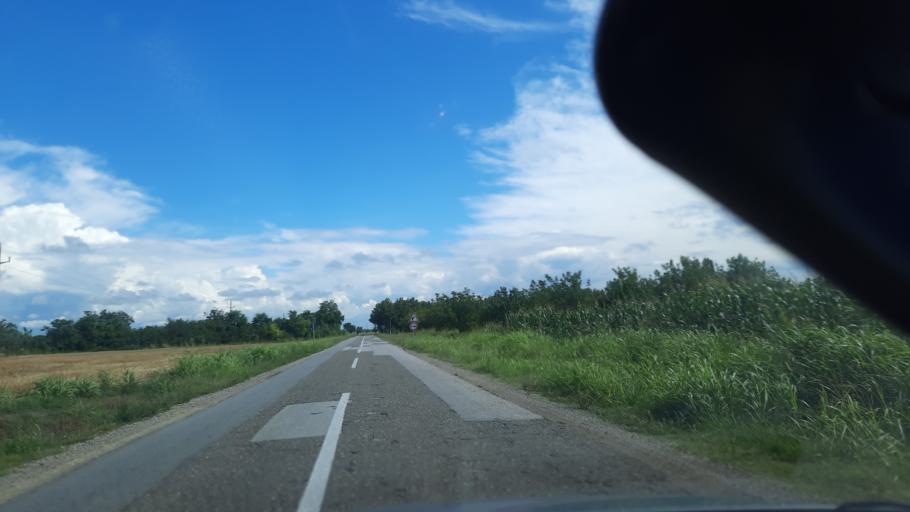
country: RS
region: Autonomna Pokrajina Vojvodina
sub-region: Sremski Okrug
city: Sremska Mitrovica
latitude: 45.0398
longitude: 19.6123
